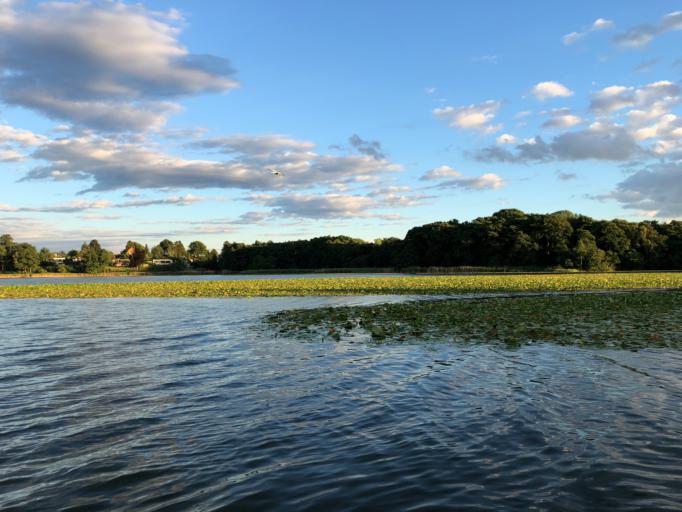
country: DK
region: Capital Region
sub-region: Gladsaxe Municipality
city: Buddinge
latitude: 55.7765
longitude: 12.4760
